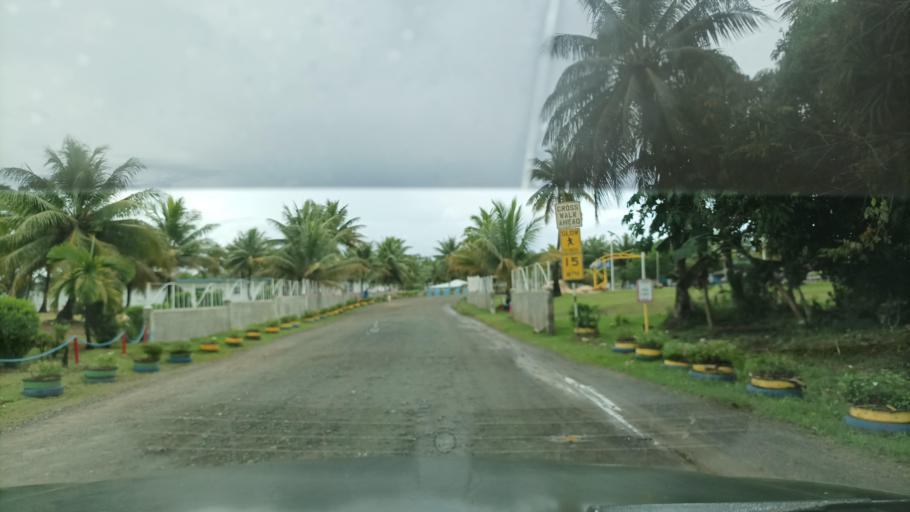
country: FM
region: Yap
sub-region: Weloy Municipality
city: Colonia
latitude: 9.5482
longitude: 138.1611
